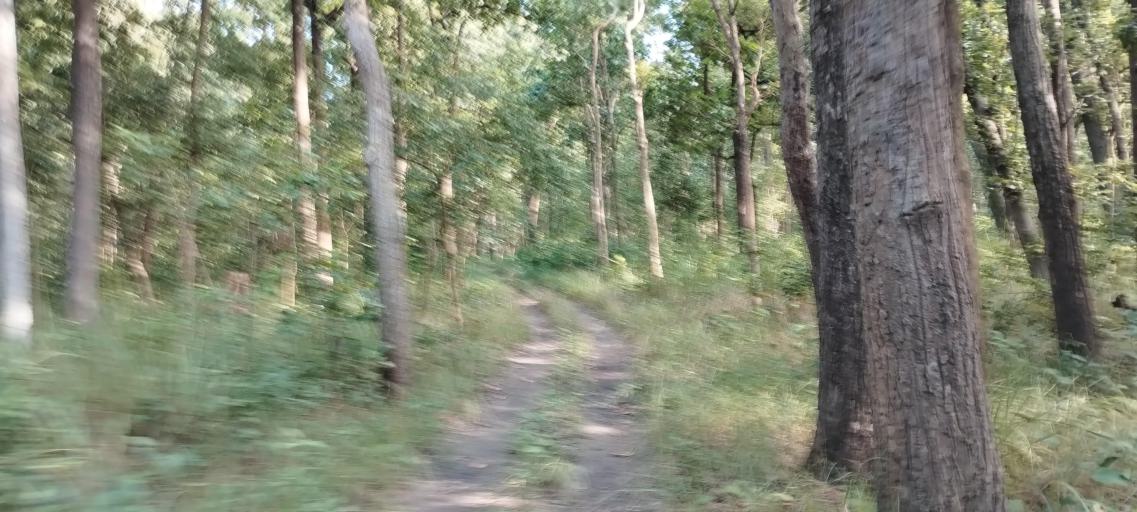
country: NP
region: Far Western
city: Tikapur
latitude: 28.5497
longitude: 81.2874
